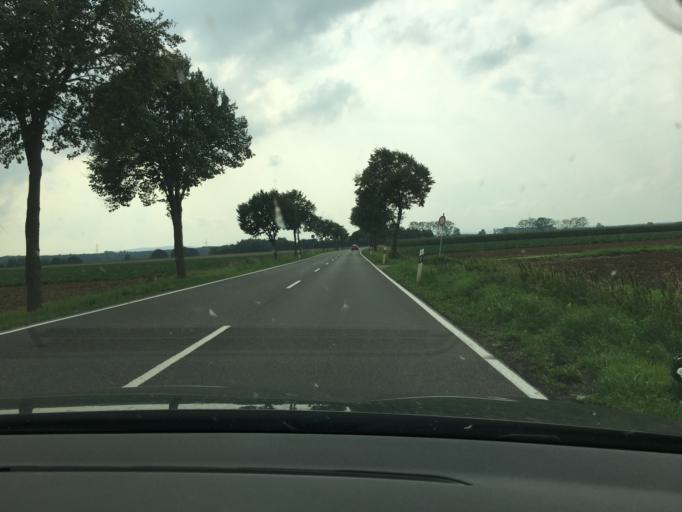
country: DE
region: North Rhine-Westphalia
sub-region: Regierungsbezirk Koln
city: Vettweiss
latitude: 50.7601
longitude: 6.5545
